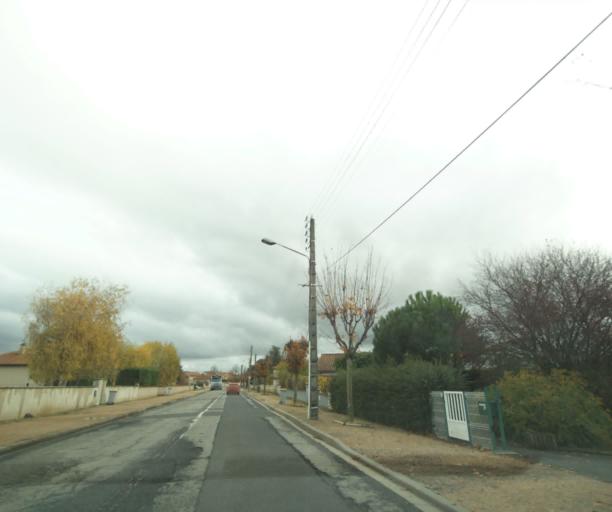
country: FR
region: Auvergne
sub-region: Departement du Puy-de-Dome
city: Pont-du-Chateau
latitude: 45.8055
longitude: 3.2454
